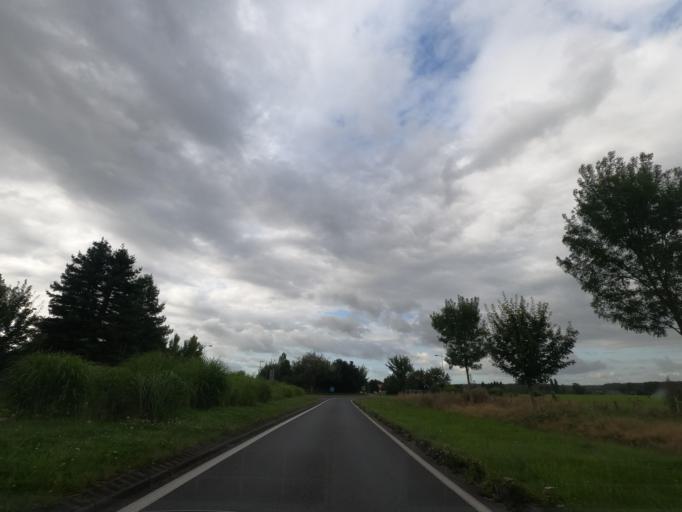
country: FR
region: Haute-Normandie
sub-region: Departement de l'Eure
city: Bourgtheroulde-Infreville
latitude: 49.3020
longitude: 0.8834
